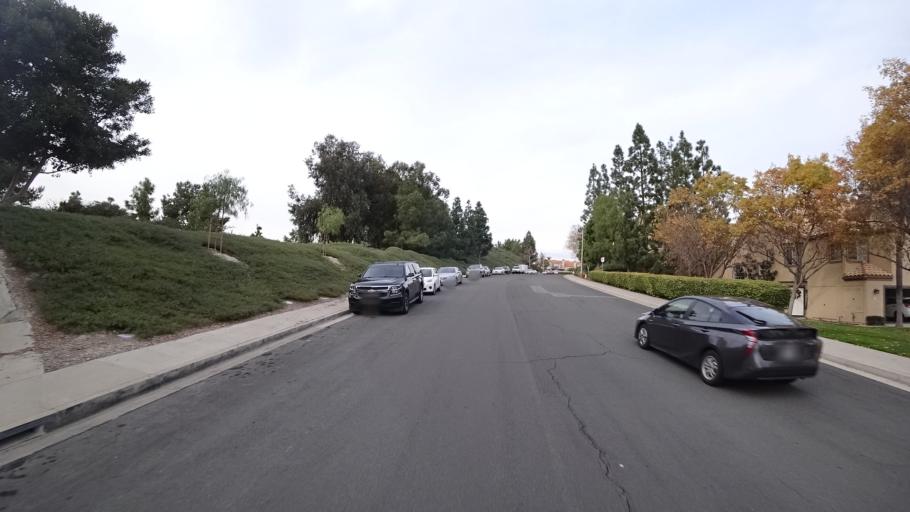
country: US
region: California
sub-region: Orange County
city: Laguna Woods
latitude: 33.5967
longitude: -117.7225
